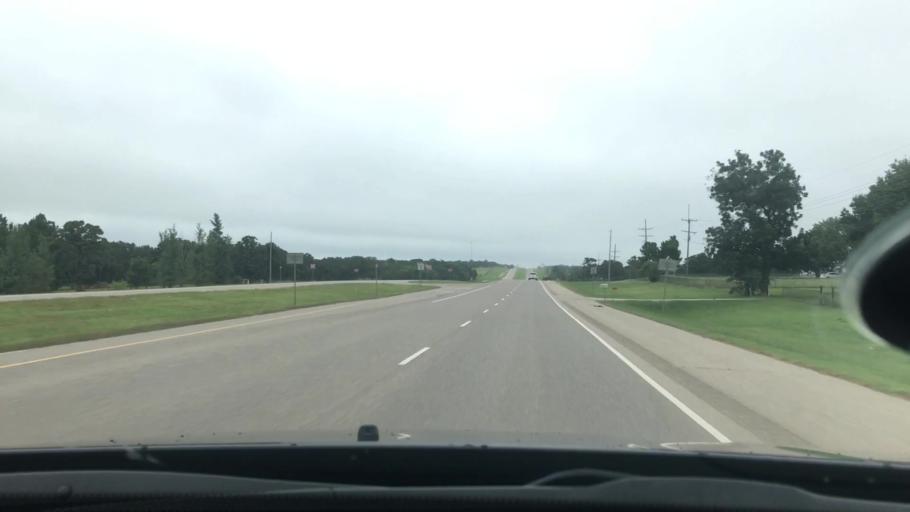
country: US
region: Oklahoma
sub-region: Seminole County
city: Seminole
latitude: 35.3536
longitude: -96.6715
